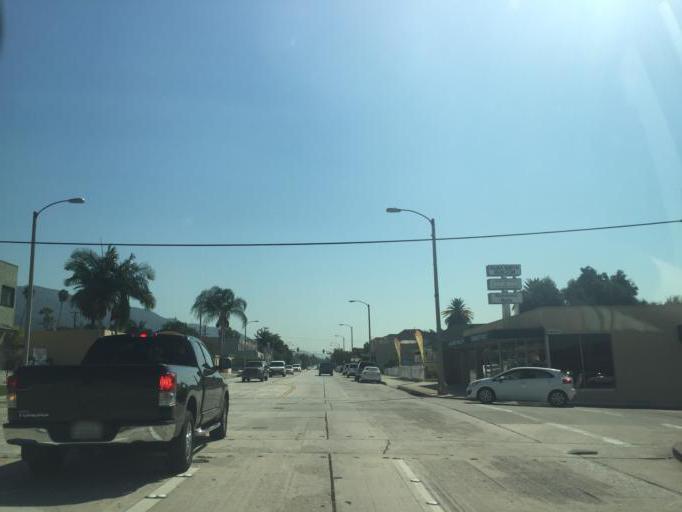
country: US
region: California
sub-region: Los Angeles County
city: Monrovia
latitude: 34.1512
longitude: -118.0078
